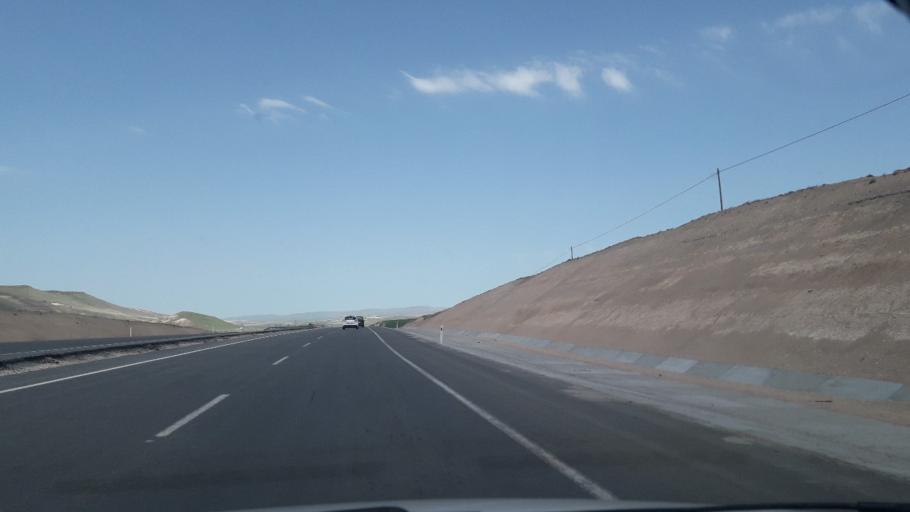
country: TR
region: Sivas
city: Deliktas
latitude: 39.2037
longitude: 37.2211
